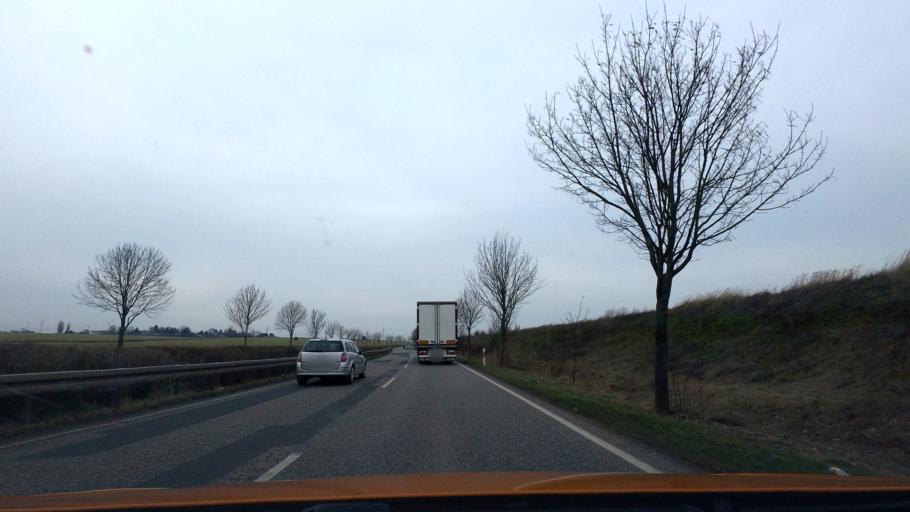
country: DE
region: Saxony-Anhalt
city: Diesdorf
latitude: 52.1416
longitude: 11.5685
